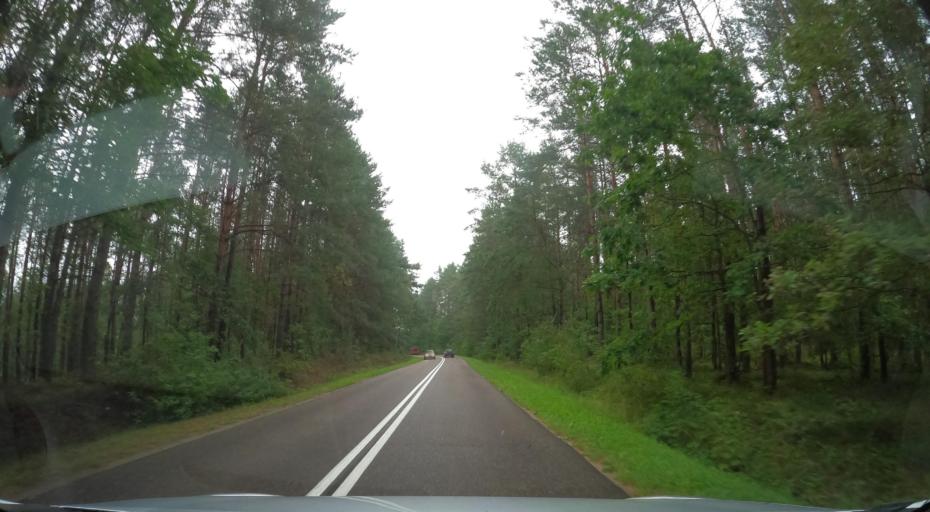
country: PL
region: Pomeranian Voivodeship
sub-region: Powiat wejherowski
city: Luzino
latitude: 54.4789
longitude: 18.0956
